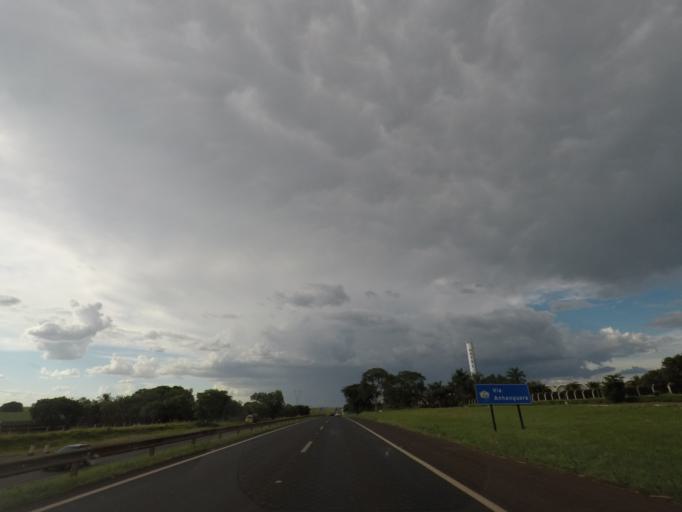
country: BR
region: Sao Paulo
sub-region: Jardinopolis
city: Jardinopolis
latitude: -21.0437
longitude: -47.8285
